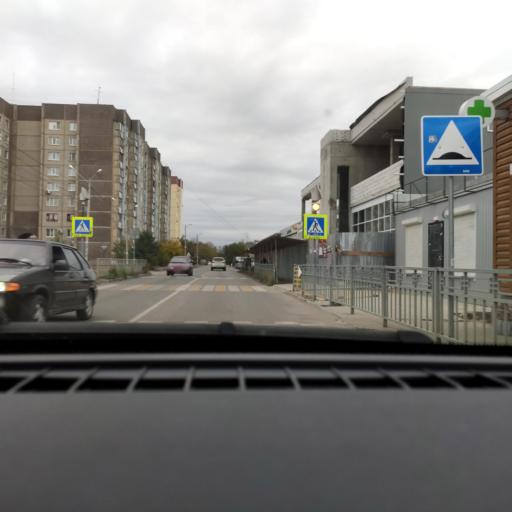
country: RU
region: Voronezj
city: Somovo
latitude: 51.7361
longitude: 39.2912
